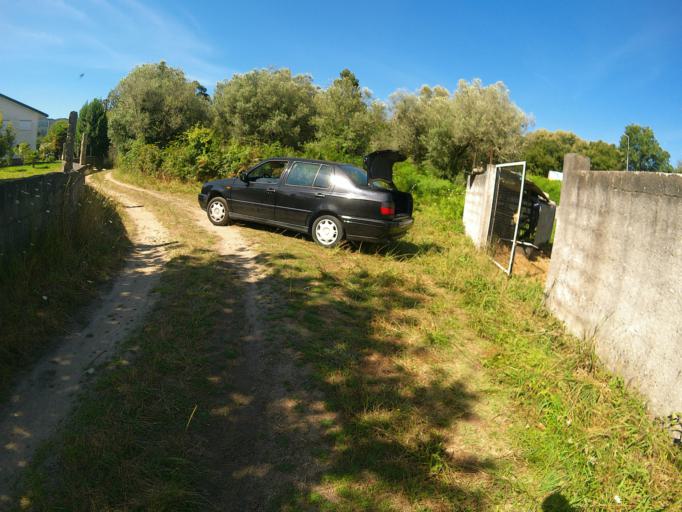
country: PT
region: Viana do Castelo
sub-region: Viana do Castelo
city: Darque
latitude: 41.7182
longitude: -8.6811
